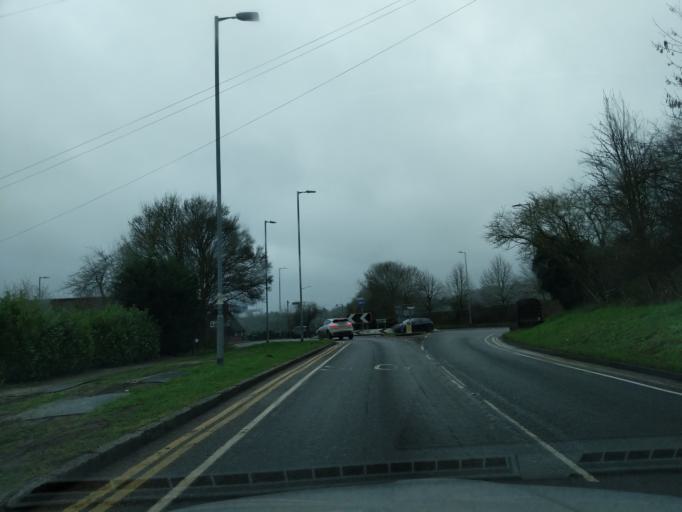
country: GB
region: England
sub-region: Hertfordshire
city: Kings Langley
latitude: 51.7066
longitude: -0.4460
